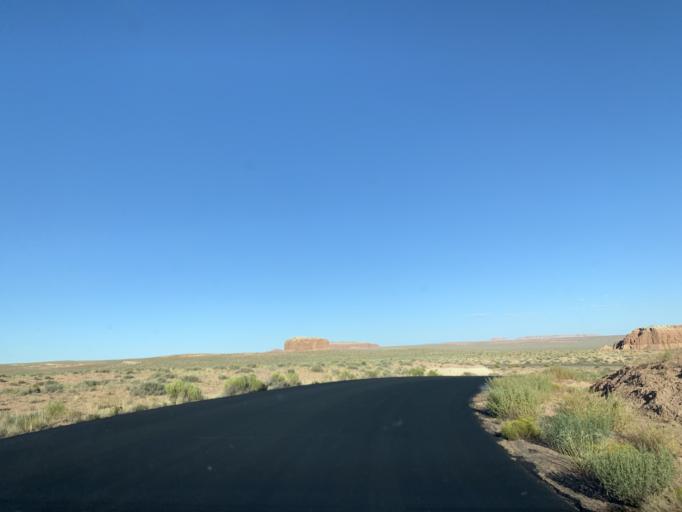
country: US
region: Utah
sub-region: Emery County
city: Ferron
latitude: 38.5722
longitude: -110.7100
